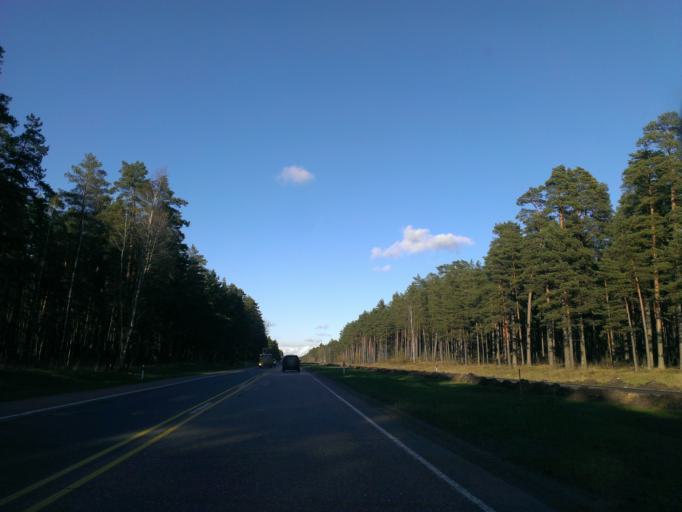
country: LV
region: Adazi
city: Adazi
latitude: 57.0233
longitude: 24.3490
